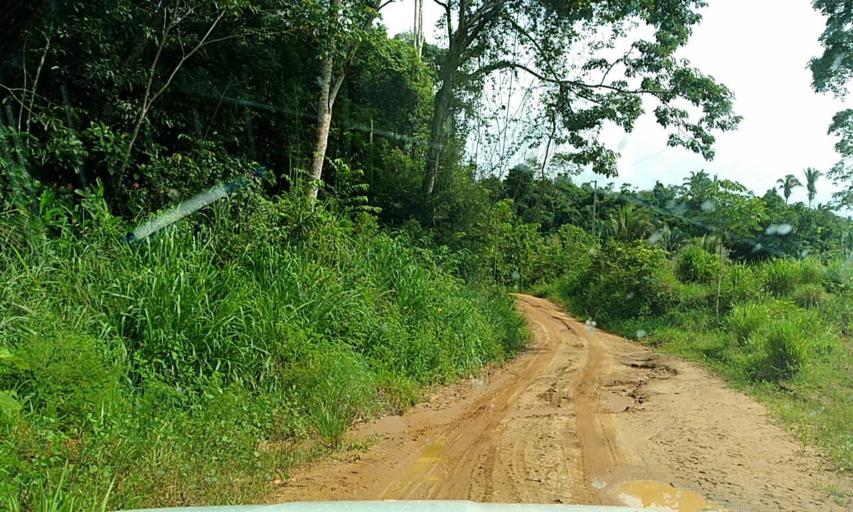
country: BR
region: Para
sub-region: Altamira
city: Altamira
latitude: -3.2224
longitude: -52.7480
